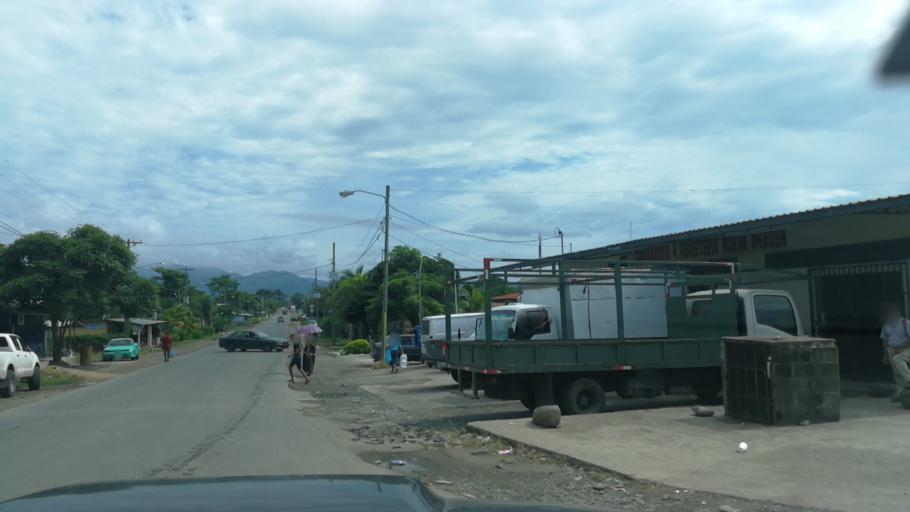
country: PA
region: Panama
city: Paso Blanco
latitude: 9.1221
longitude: -79.2521
